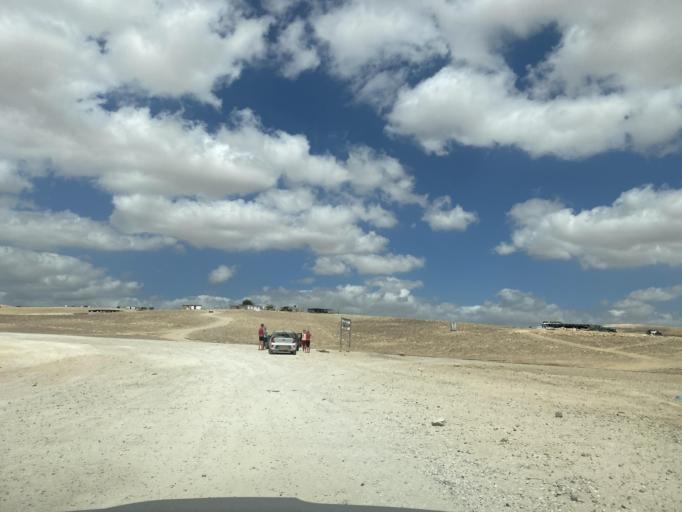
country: PS
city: `Arab ar Rashaydah
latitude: 31.5328
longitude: 35.2841
